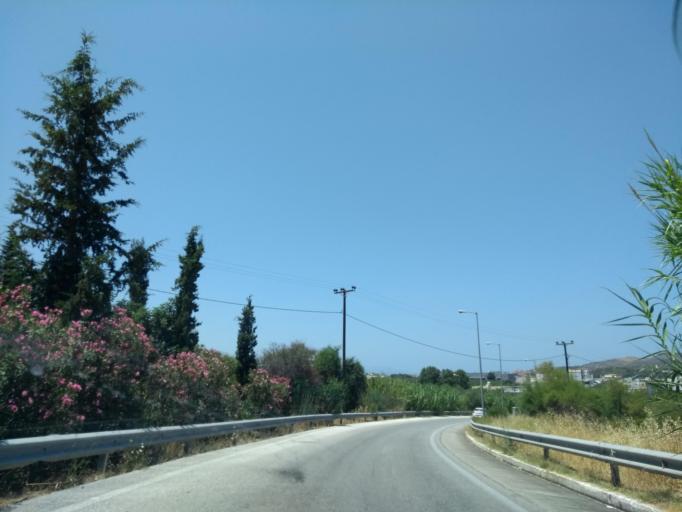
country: GR
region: Crete
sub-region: Nomos Chanias
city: Tsikalaria
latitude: 35.4809
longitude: 24.0642
